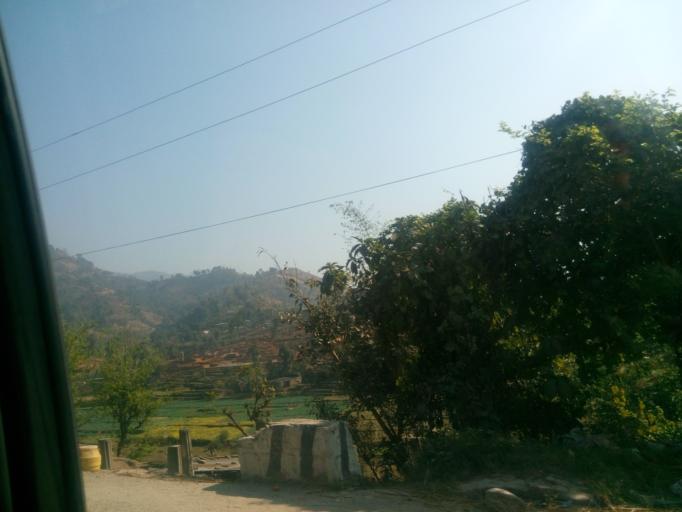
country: NP
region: Central Region
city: Kirtipur
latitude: 27.7535
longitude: 85.0447
